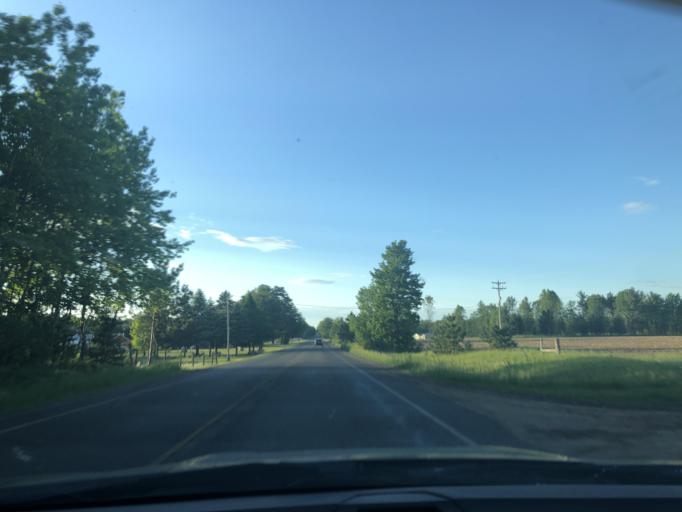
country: US
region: Michigan
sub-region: Missaukee County
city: Lake City
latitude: 44.3798
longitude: -85.0758
